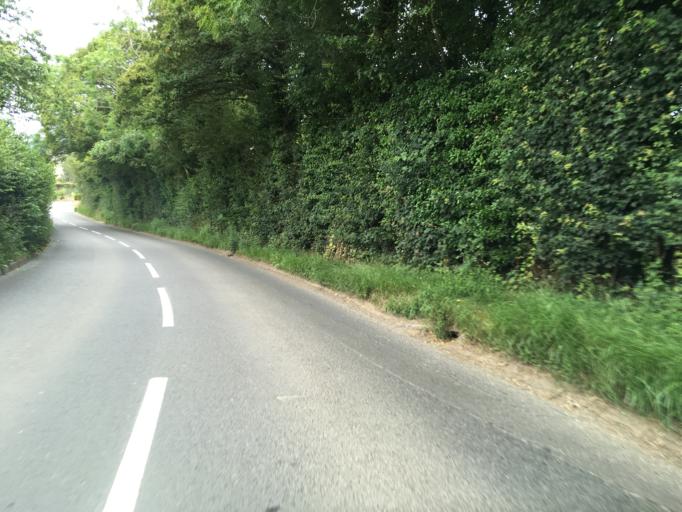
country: GB
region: England
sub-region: Gloucestershire
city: Bourton on the Water
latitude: 51.8760
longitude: -1.7186
